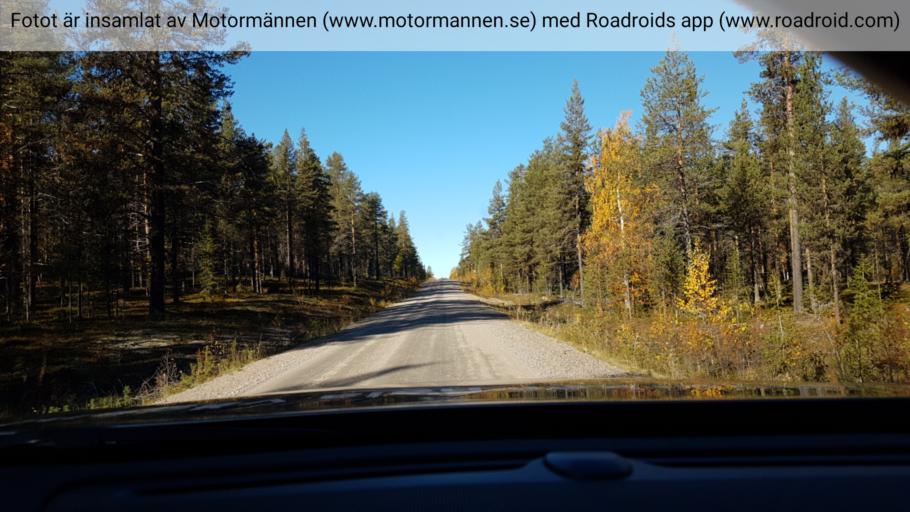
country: SE
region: Norrbotten
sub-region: Gallivare Kommun
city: Gaellivare
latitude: 66.6429
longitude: 21.0063
